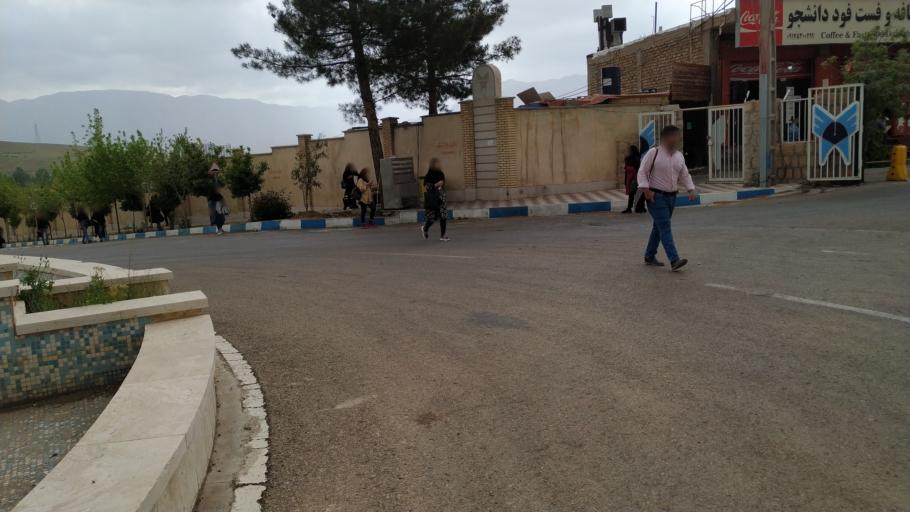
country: IR
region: Fars
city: Shiraz
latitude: 29.7675
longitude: 52.4804
